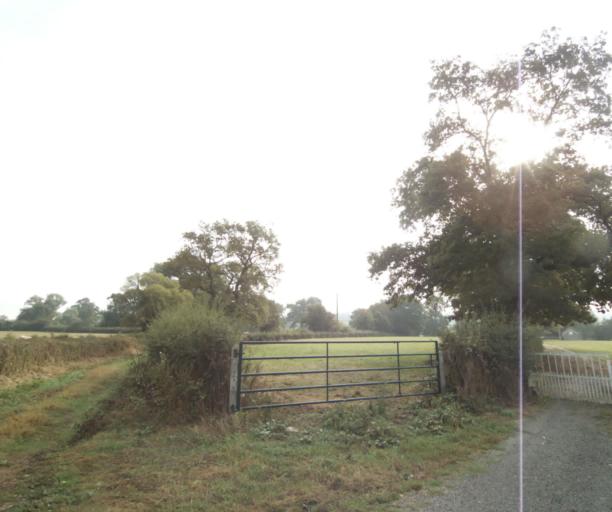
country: FR
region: Bourgogne
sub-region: Departement de Saone-et-Loire
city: Charolles
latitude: 46.4580
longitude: 4.3022
